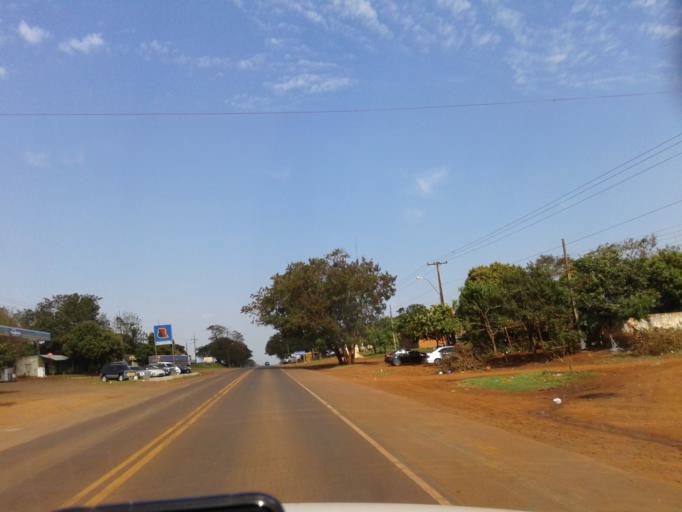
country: PY
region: Alto Parana
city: Colonia Yguazu
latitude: -25.5019
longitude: -54.8987
